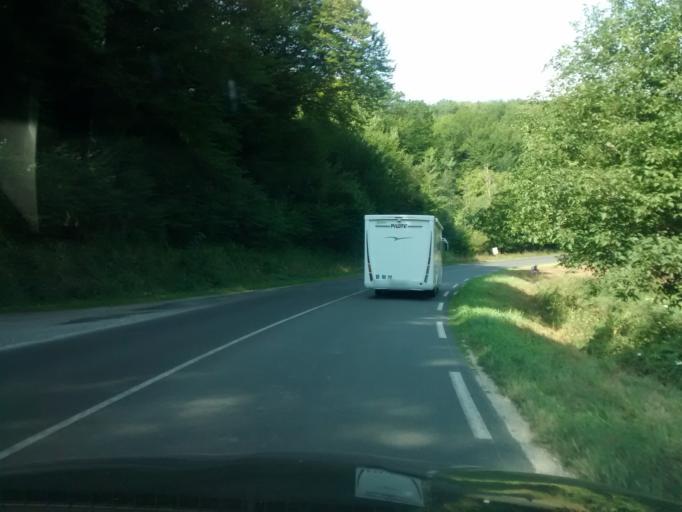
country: FR
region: Aquitaine
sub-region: Departement de la Dordogne
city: Cenac-et-Saint-Julien
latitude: 44.8453
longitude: 1.1773
